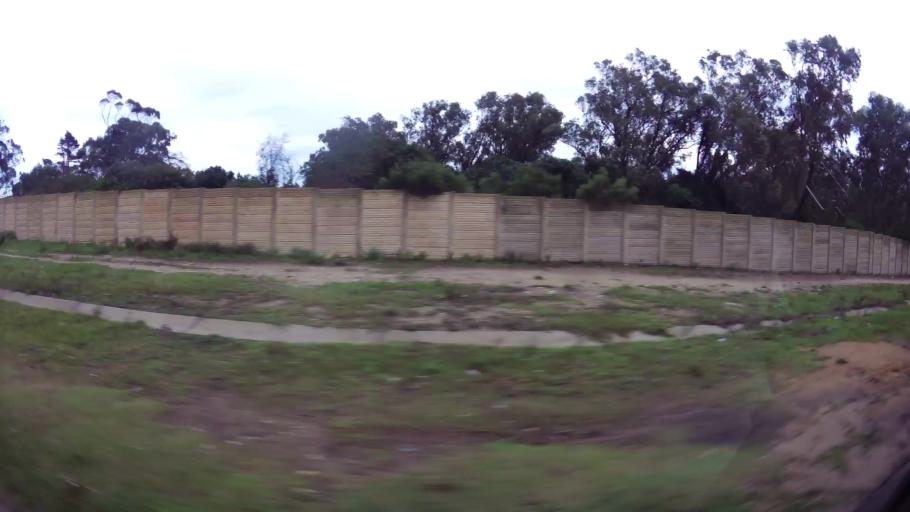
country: ZA
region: Eastern Cape
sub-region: Nelson Mandela Bay Metropolitan Municipality
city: Port Elizabeth
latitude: -33.9927
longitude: 25.5793
